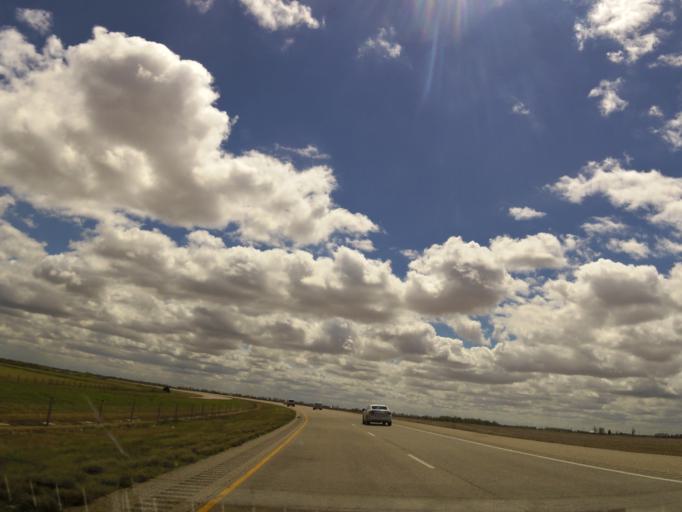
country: US
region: Arkansas
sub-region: Craighead County
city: Bay
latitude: 35.7183
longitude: -90.5801
